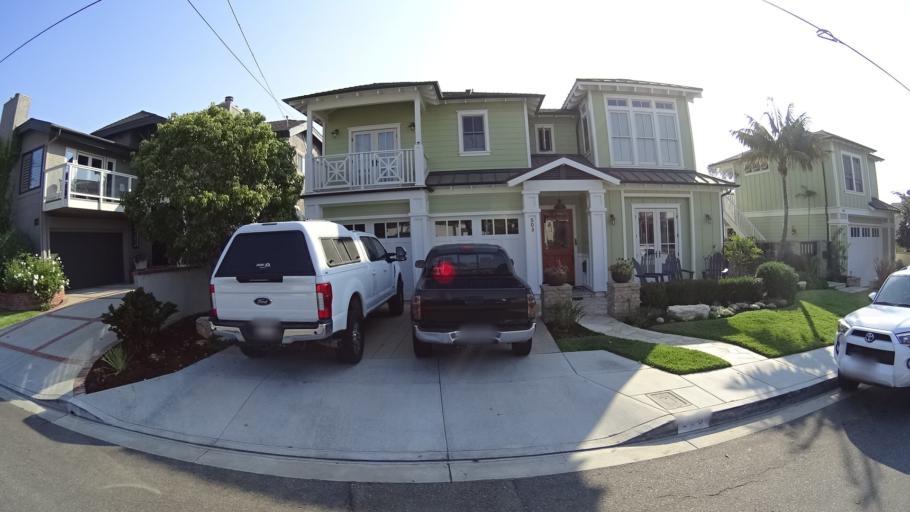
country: US
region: California
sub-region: Orange County
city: San Clemente
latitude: 33.4117
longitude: -117.6093
